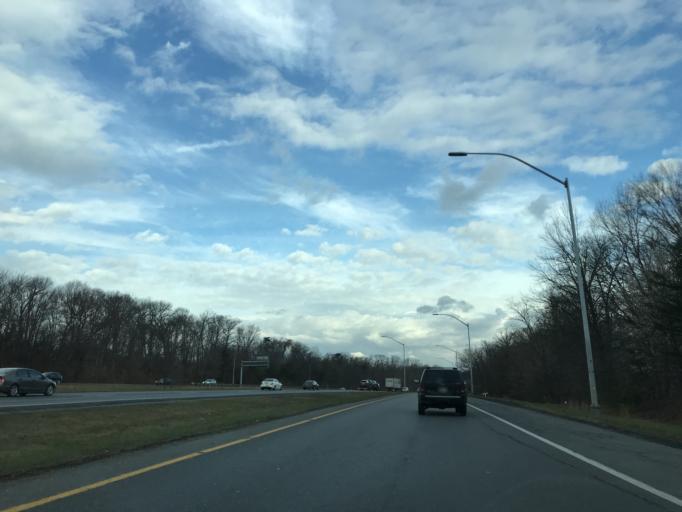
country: US
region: Maryland
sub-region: Howard County
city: Savage
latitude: 39.1419
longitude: -76.8169
